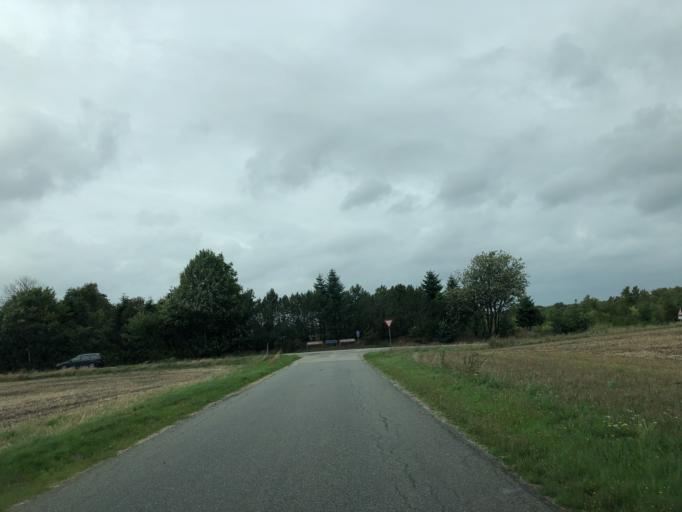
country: DK
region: Central Jutland
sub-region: Herning Kommune
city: Lind
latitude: 56.0893
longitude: 8.9539
